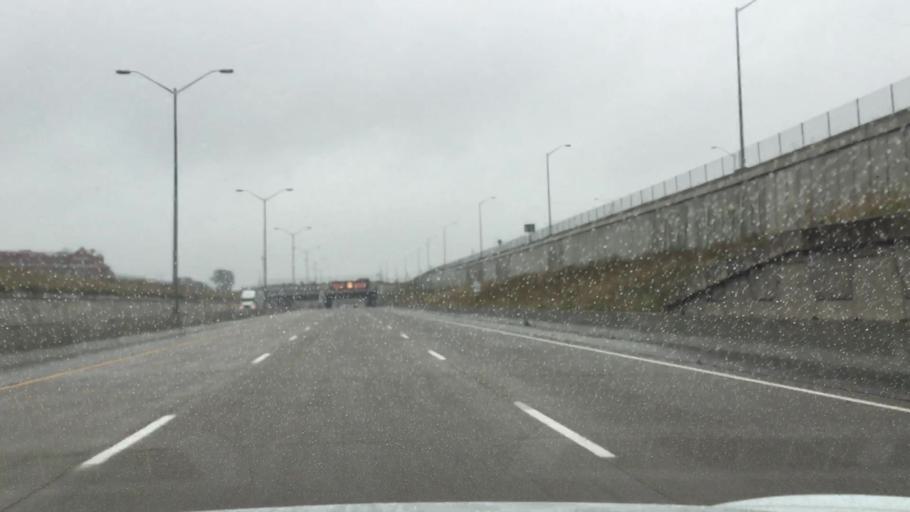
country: CA
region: Ontario
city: Windsor
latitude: 42.2434
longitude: -83.0185
